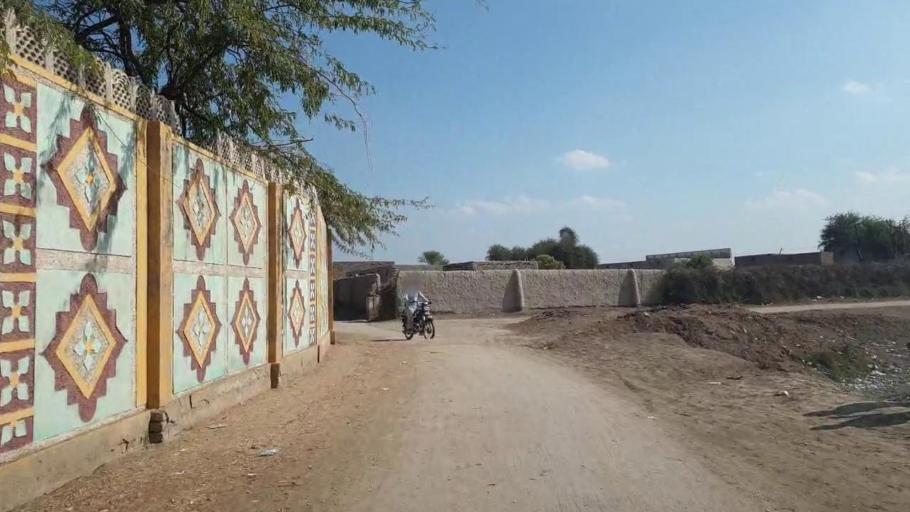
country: PK
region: Sindh
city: Shahpur Chakar
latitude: 26.0714
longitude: 68.5820
